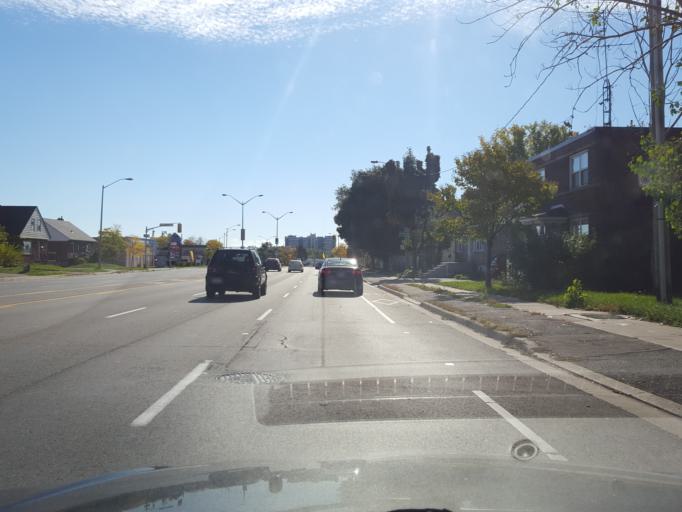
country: CA
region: Ontario
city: Burlington
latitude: 43.3398
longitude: -79.8197
